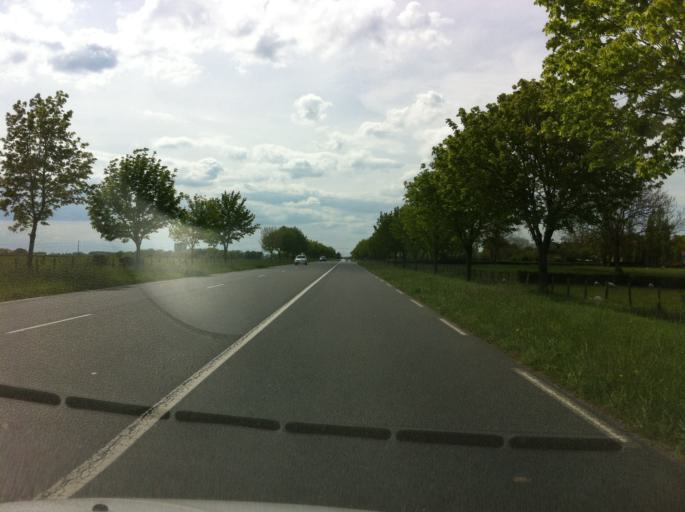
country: FR
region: Auvergne
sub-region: Departement de l'Allier
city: Chantelle
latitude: 46.3156
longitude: 3.1904
